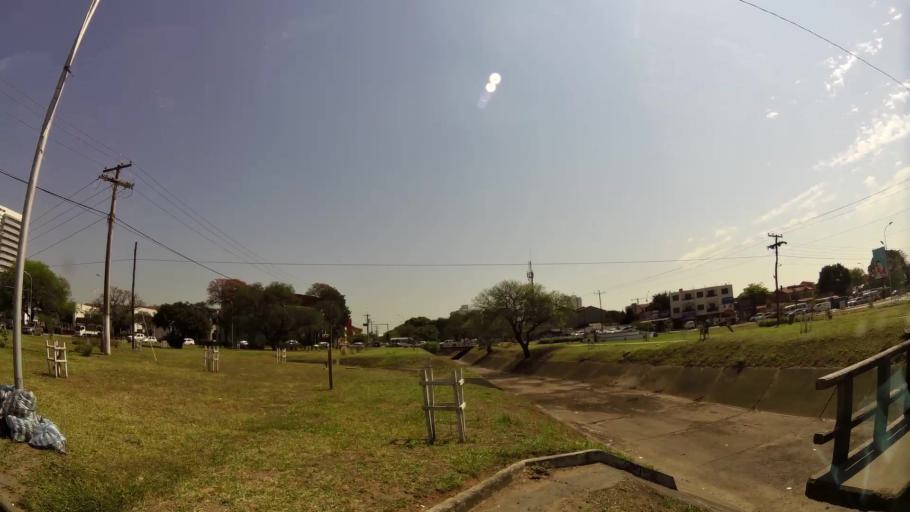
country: BO
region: Santa Cruz
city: Santa Cruz de la Sierra
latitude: -17.7522
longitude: -63.1637
